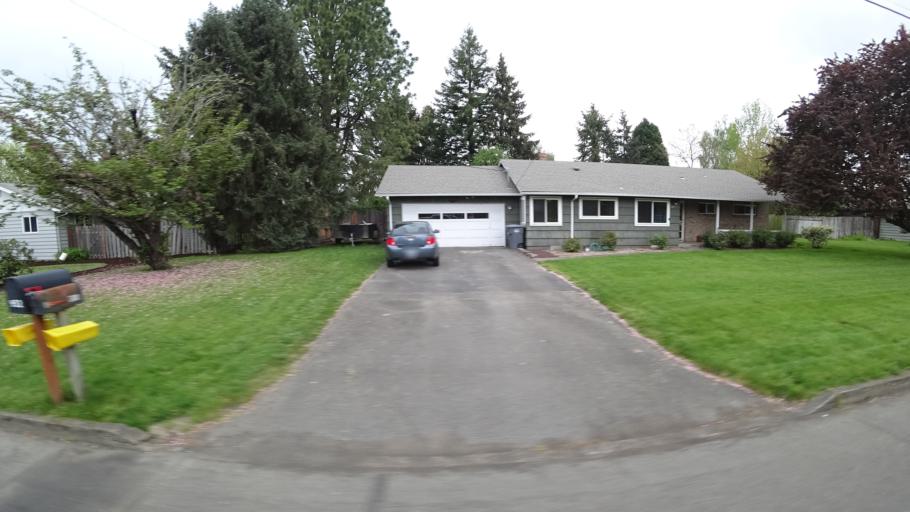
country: US
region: Oregon
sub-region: Washington County
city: Hillsboro
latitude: 45.5327
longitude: -122.9743
